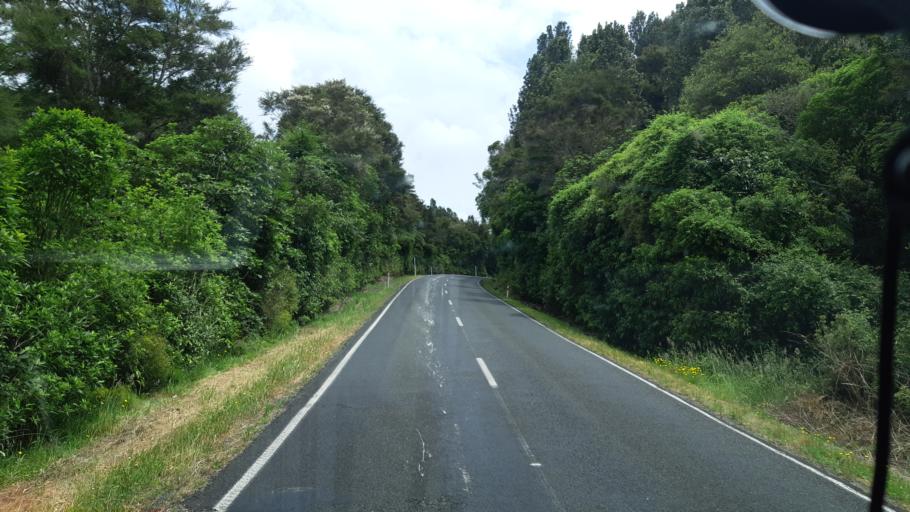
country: NZ
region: Waikato
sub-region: South Waikato District
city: Tokoroa
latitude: -38.2728
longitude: 175.6660
